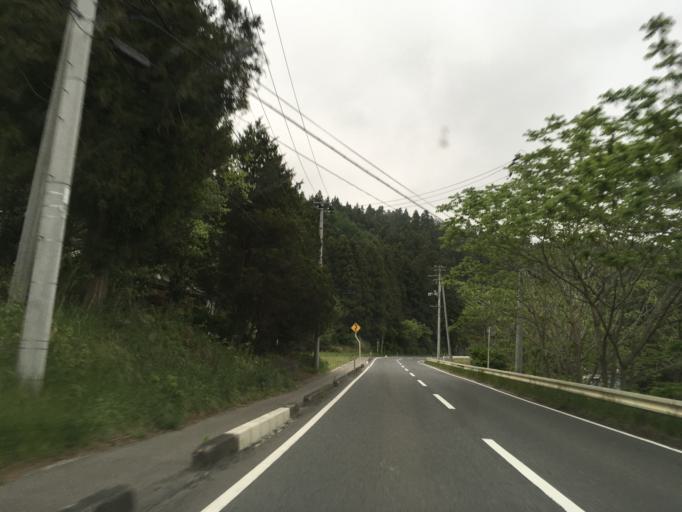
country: JP
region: Iwate
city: Ichinoseki
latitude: 38.7342
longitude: 141.3036
